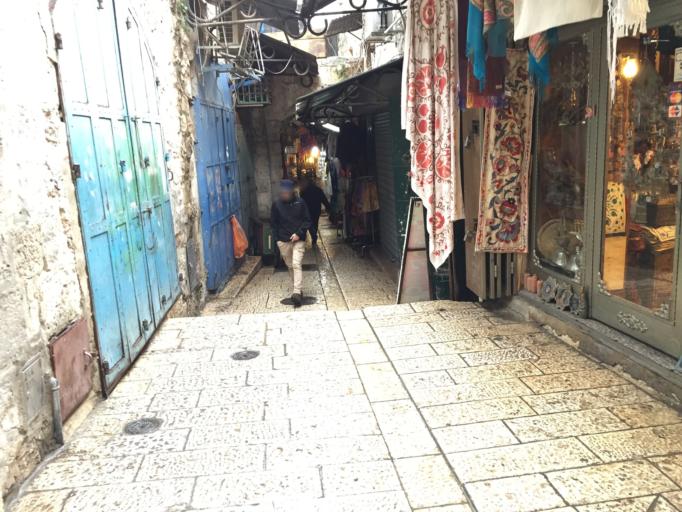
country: PS
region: West Bank
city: Old City
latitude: 31.7766
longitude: 35.2308
